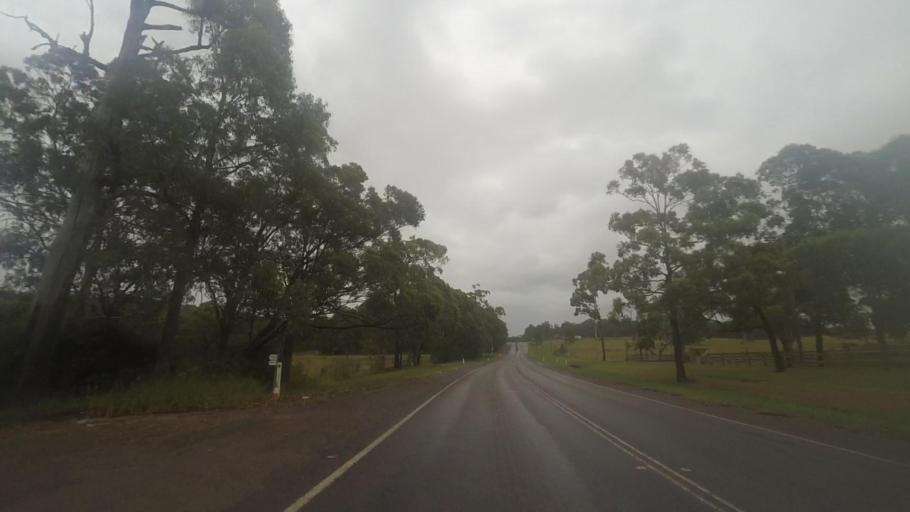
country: AU
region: New South Wales
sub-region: Port Stephens Shire
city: Medowie
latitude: -32.6536
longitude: 151.9527
